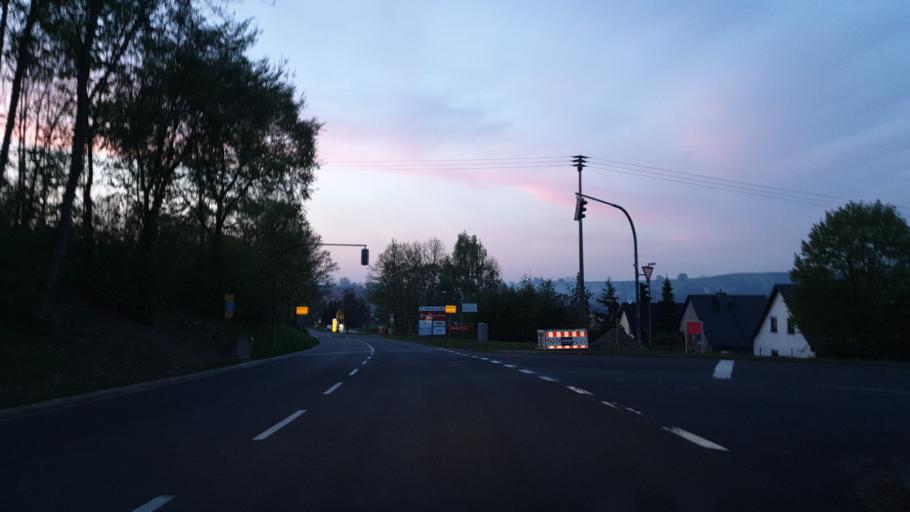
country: DE
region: Saxony
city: Stollberg
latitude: 50.7179
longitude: 12.7848
